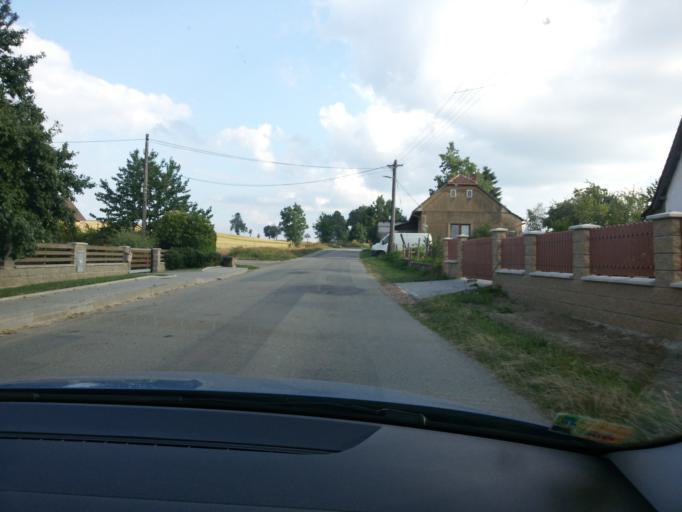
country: CZ
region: South Moravian
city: Olesnice
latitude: 49.4822
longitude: 16.4258
